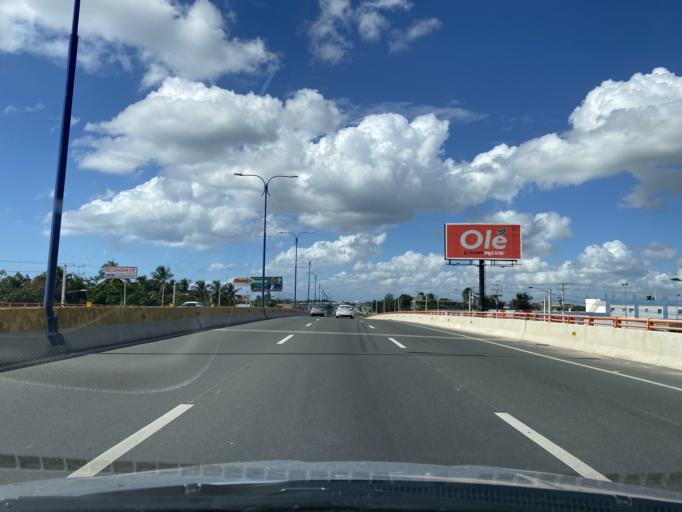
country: DO
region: Santo Domingo
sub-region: Santo Domingo
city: Boca Chica
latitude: 18.4501
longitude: -69.6714
